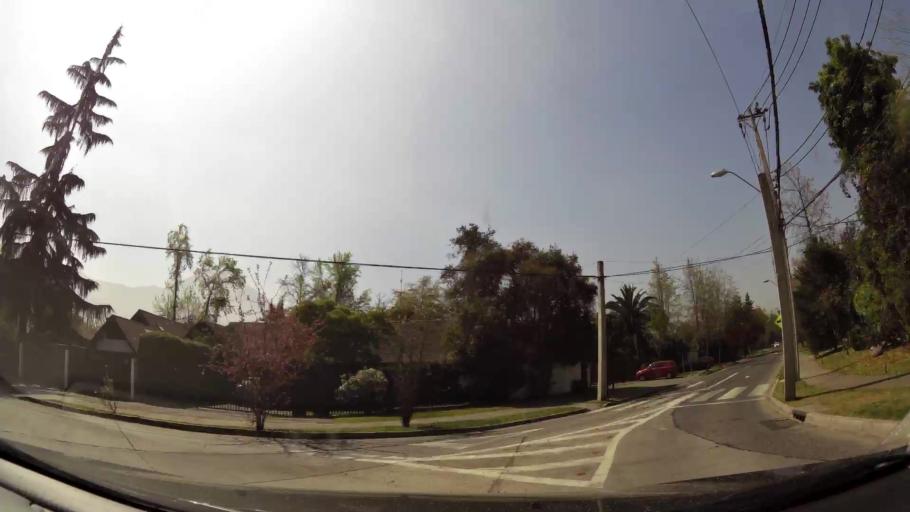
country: CL
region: Santiago Metropolitan
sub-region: Provincia de Santiago
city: Villa Presidente Frei, Nunoa, Santiago, Chile
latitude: -33.3858
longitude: -70.5832
